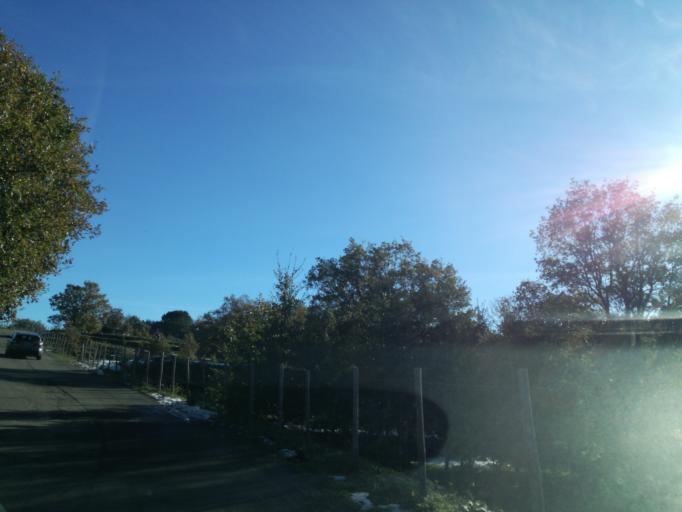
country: IT
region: Sicily
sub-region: Catania
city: Randazzo
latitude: 37.8580
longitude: 14.9823
